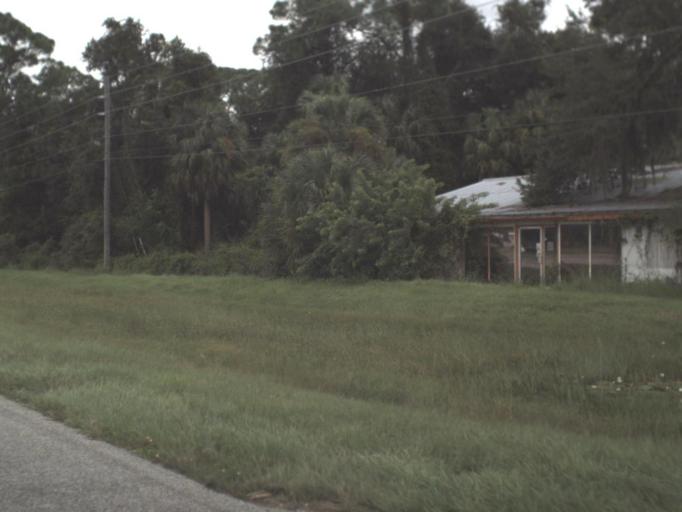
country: US
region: Florida
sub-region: Lee County
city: Alva
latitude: 26.7111
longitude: -81.6400
